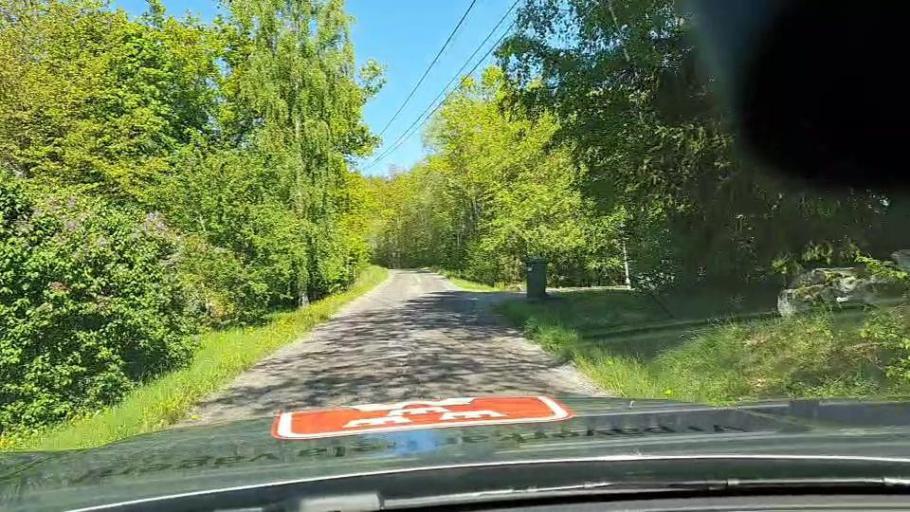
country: SE
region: Soedermanland
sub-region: Strangnas Kommun
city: Strangnas
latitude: 59.4575
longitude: 16.8889
